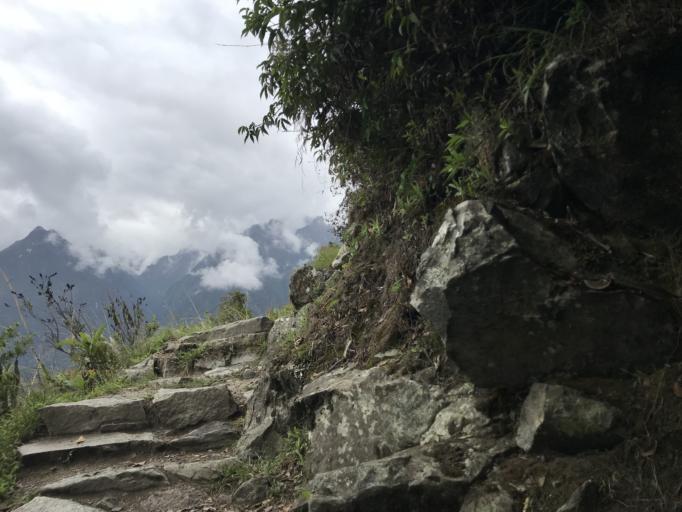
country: PE
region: Cusco
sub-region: Provincia de La Convencion
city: Santa Teresa
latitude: -13.1701
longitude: -72.5365
